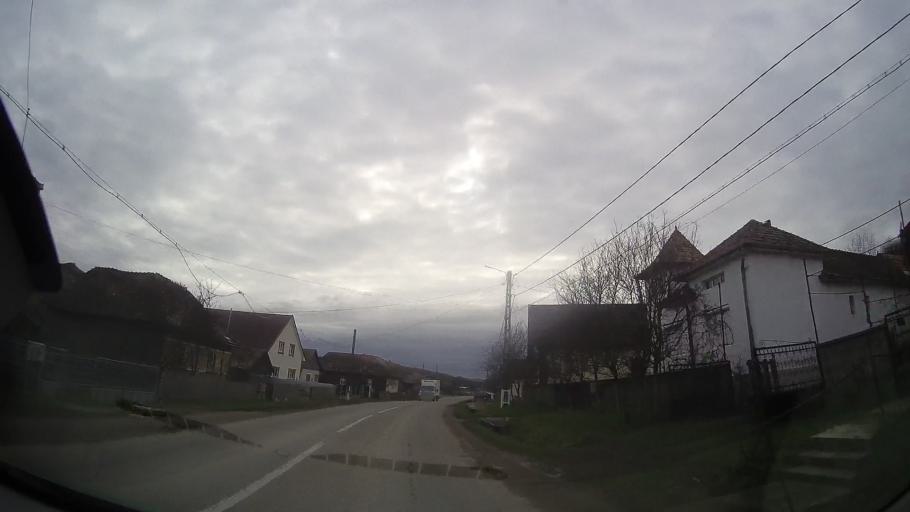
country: RO
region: Bistrita-Nasaud
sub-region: Comuna Budesti
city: Budesti
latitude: 46.8737
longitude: 24.2465
